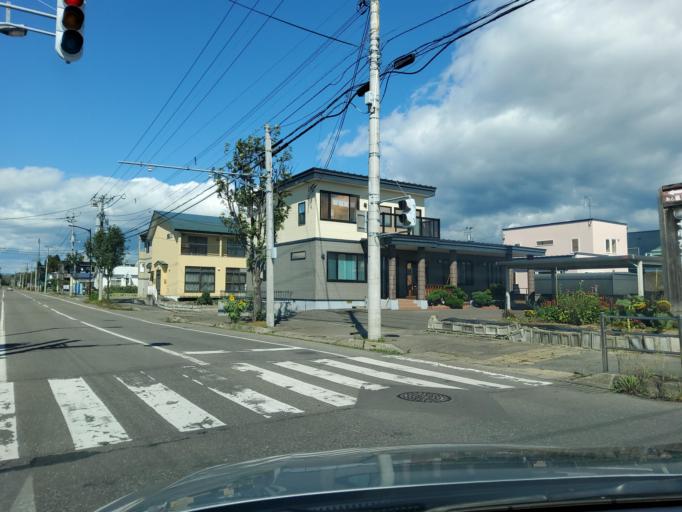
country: JP
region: Hokkaido
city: Obihiro
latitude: 42.9480
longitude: 143.2156
